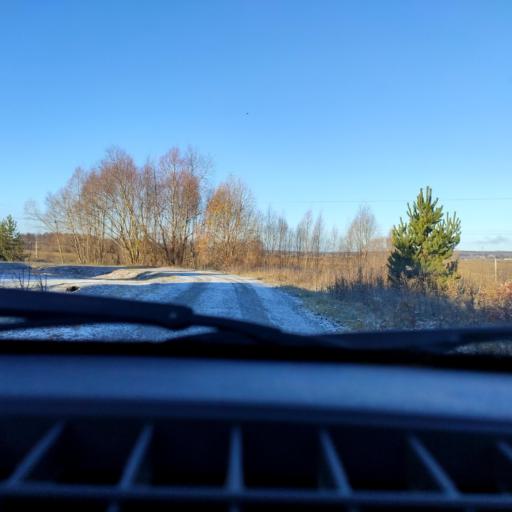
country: RU
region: Bashkortostan
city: Avdon
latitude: 54.6963
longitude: 55.7889
